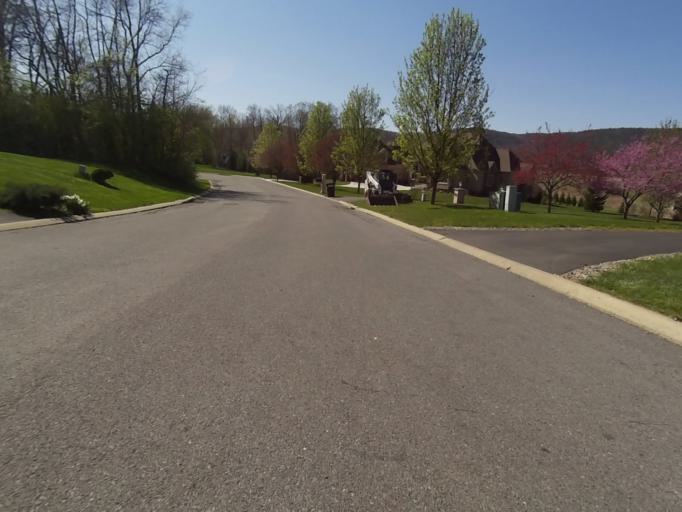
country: US
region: Pennsylvania
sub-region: Centre County
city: Houserville
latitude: 40.8807
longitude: -77.8277
